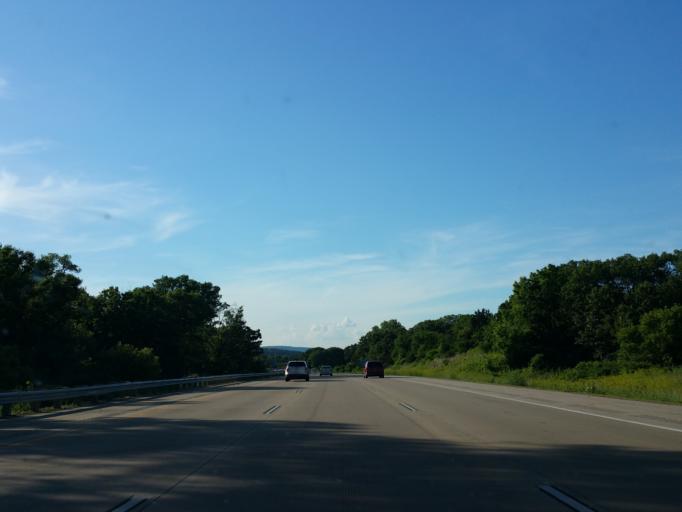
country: US
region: Wisconsin
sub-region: Columbia County
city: Poynette
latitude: 43.3826
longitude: -89.4622
